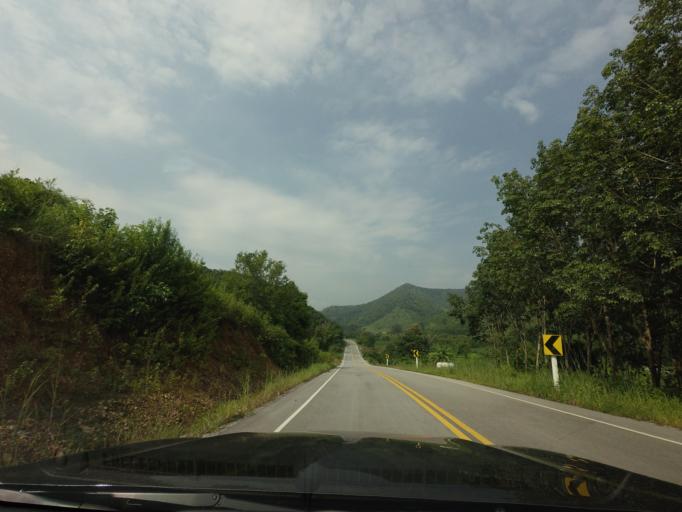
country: TH
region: Loei
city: Chiang Khan
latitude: 17.7859
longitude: 101.5509
